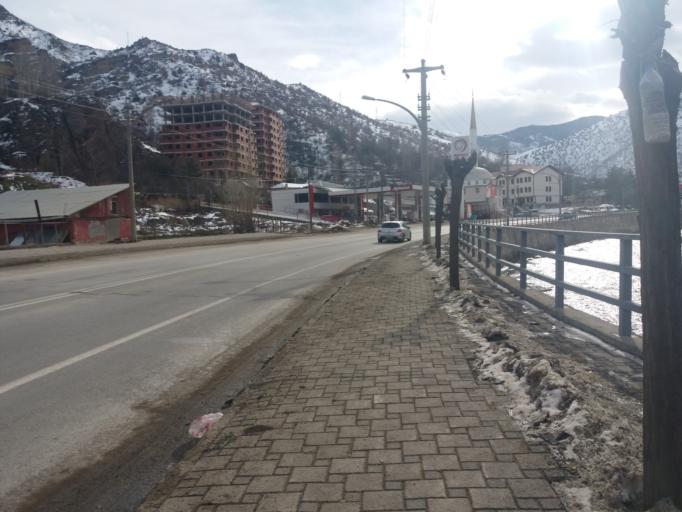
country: TR
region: Gumushane
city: Gumushkhane
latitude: 40.4455
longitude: 39.5034
